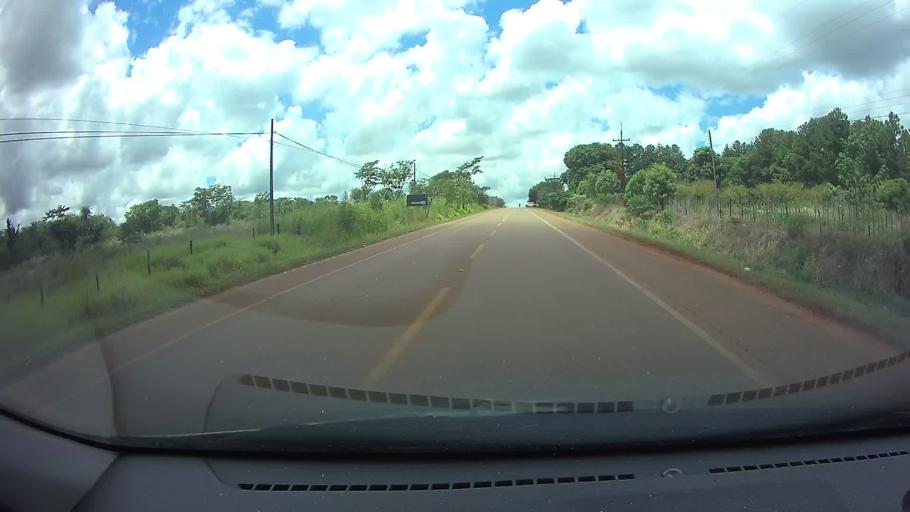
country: PY
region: Paraguari
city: La Colmena
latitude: -25.8915
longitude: -56.8267
